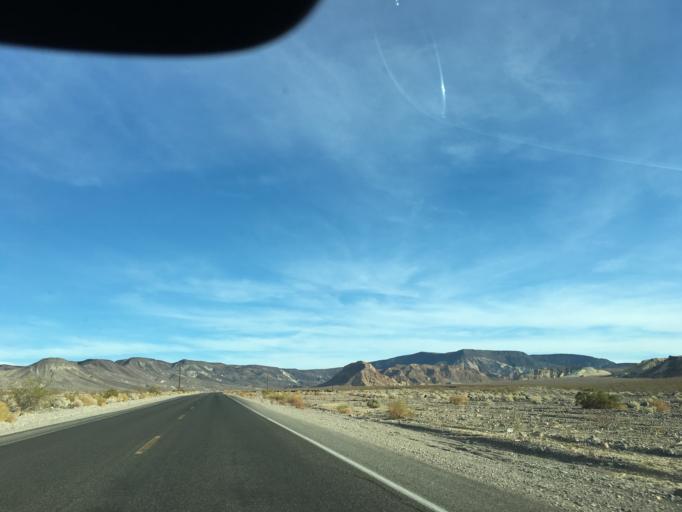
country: US
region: Nevada
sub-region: Nye County
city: Beatty
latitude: 36.3631
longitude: -116.7203
